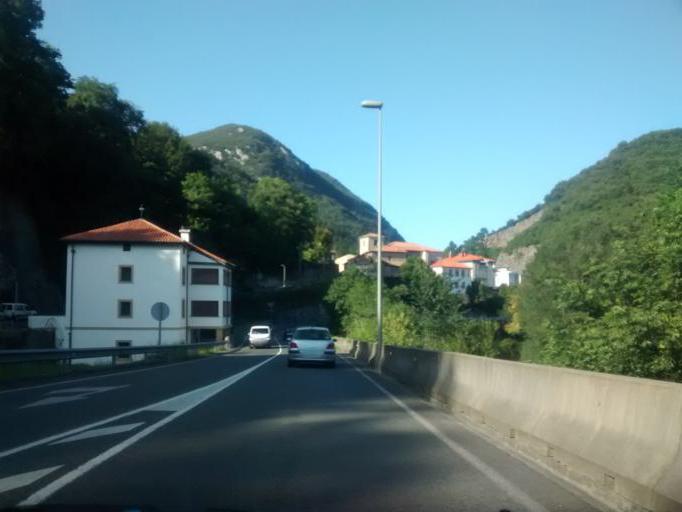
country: ES
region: Basque Country
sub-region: Provincia de Guipuzcoa
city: Mendaro
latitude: 43.2515
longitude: -2.3899
